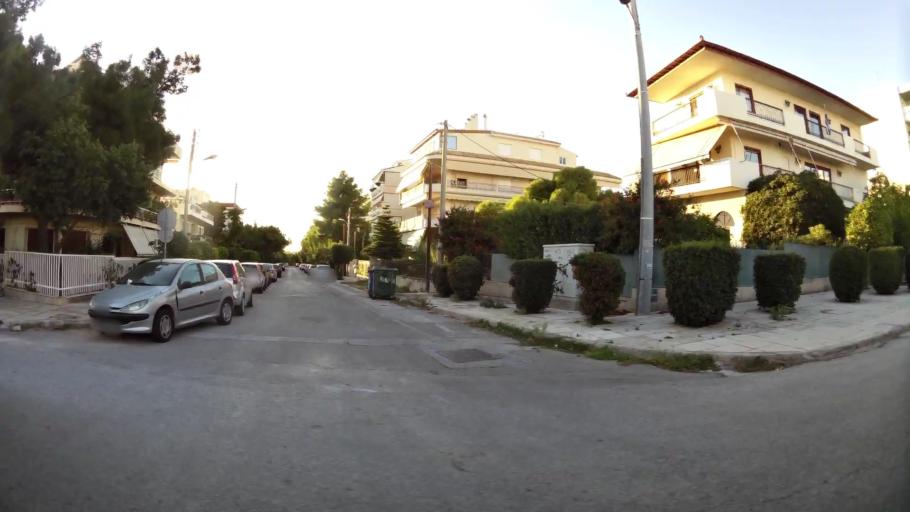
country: GR
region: Attica
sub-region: Nomarchia Athinas
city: Glyfada
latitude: 37.8765
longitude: 23.7522
